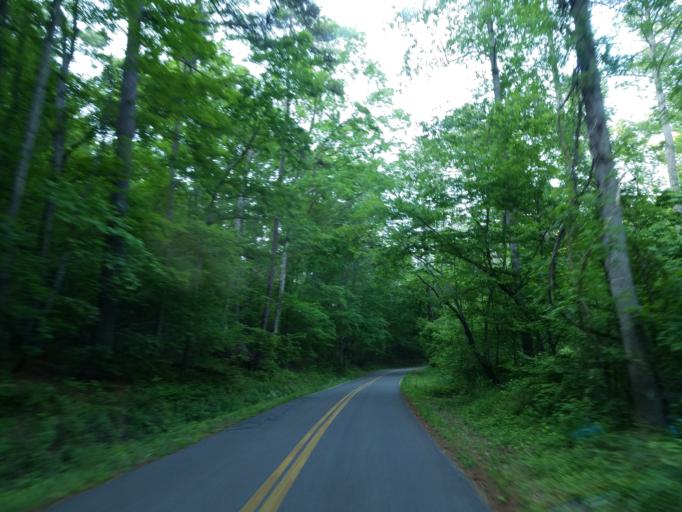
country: US
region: Georgia
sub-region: Gordon County
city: Calhoun
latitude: 34.5627
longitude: -85.1024
